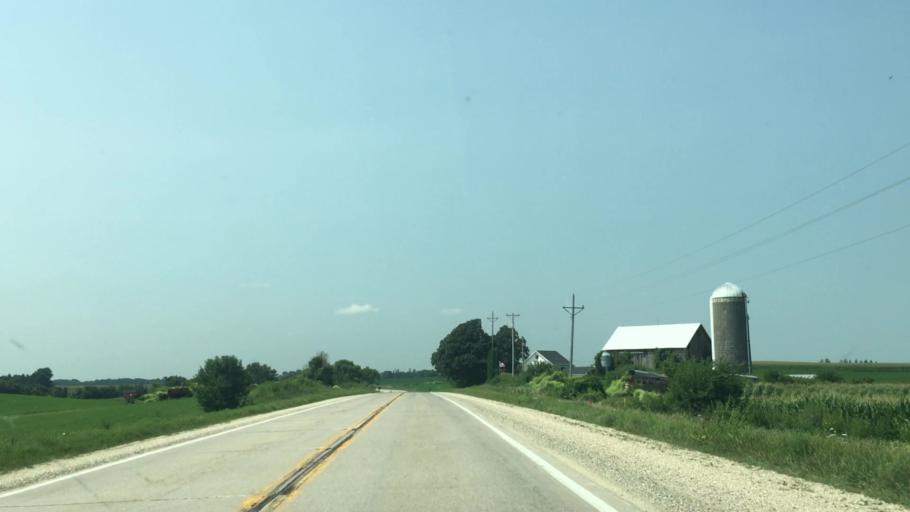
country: US
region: Iowa
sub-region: Fayette County
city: West Union
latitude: 43.0906
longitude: -91.8539
